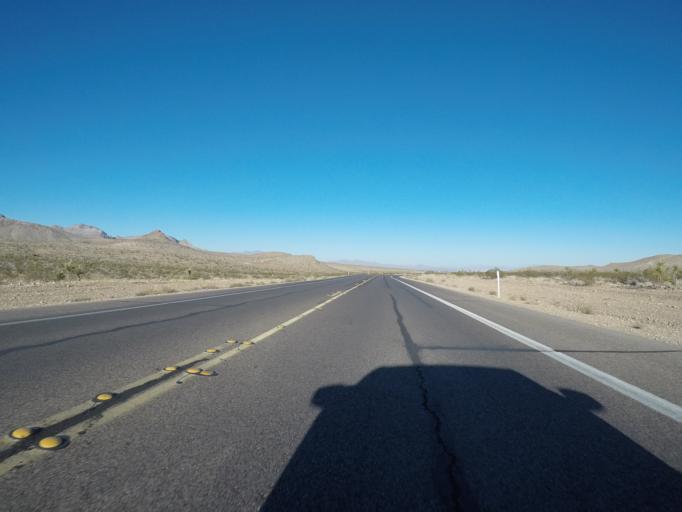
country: US
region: Nevada
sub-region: Clark County
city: Summerlin South
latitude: 36.1394
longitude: -115.4040
